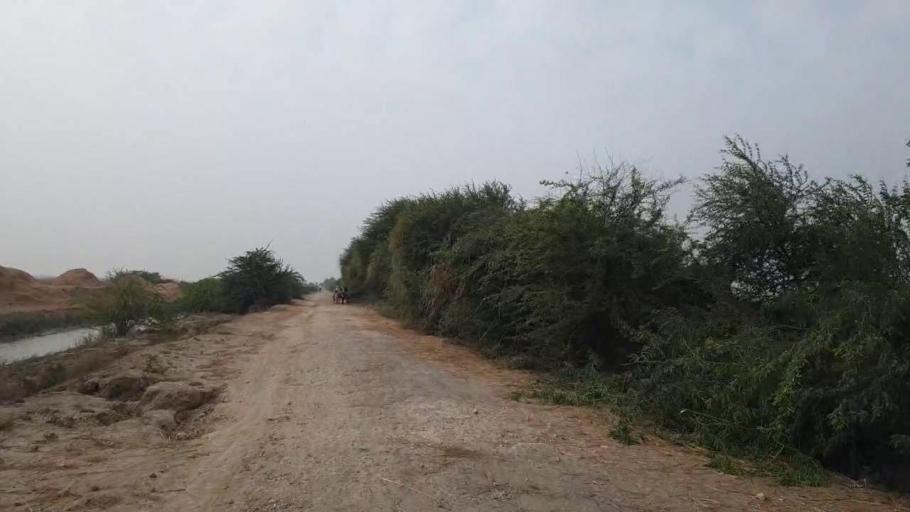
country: PK
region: Sindh
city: Kario
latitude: 24.9044
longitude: 68.5323
